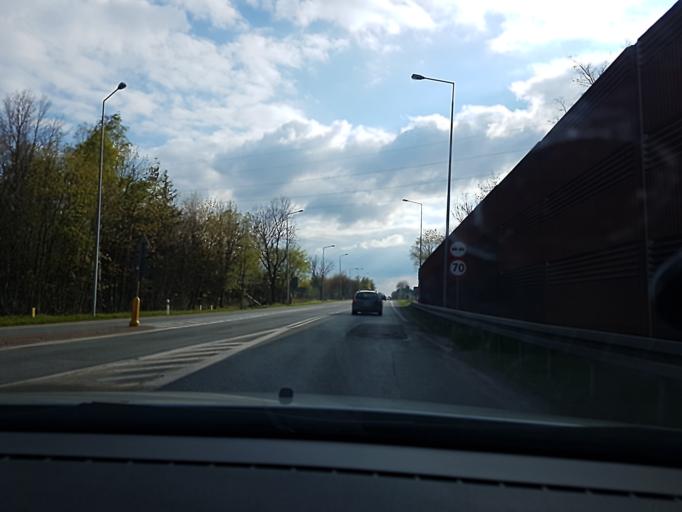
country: PL
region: Masovian Voivodeship
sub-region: Powiat sochaczewski
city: Sochaczew
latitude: 52.2190
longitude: 20.2038
